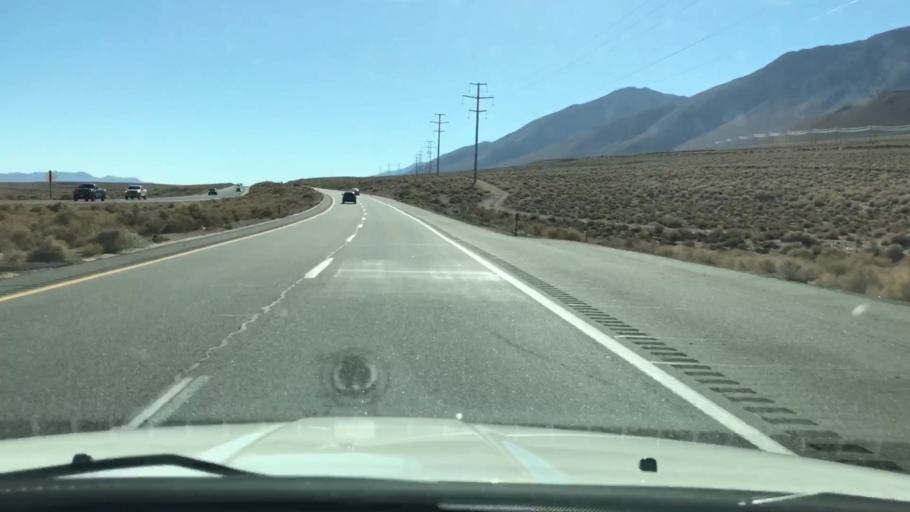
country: US
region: California
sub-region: Inyo County
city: Lone Pine
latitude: 36.4650
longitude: -118.0367
